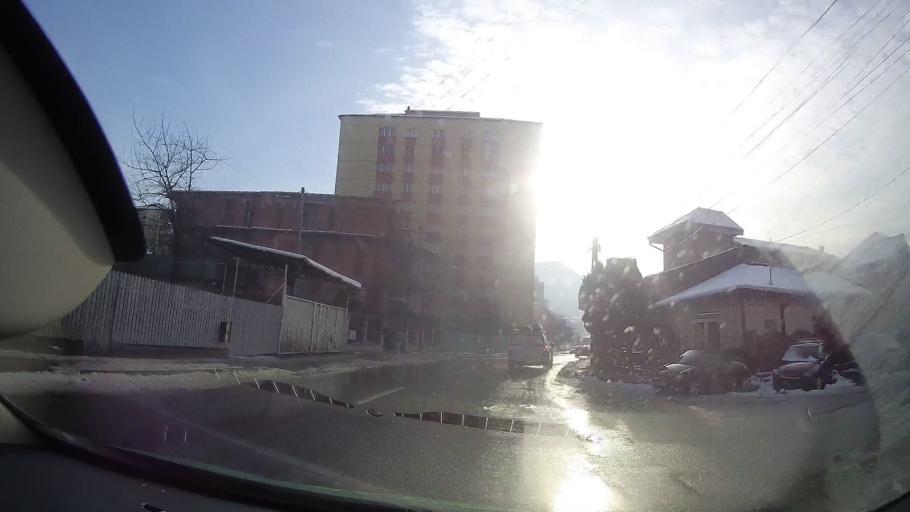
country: RO
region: Neamt
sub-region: Municipiul Piatra-Neamt
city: Valeni
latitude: 46.9406
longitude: 26.3820
